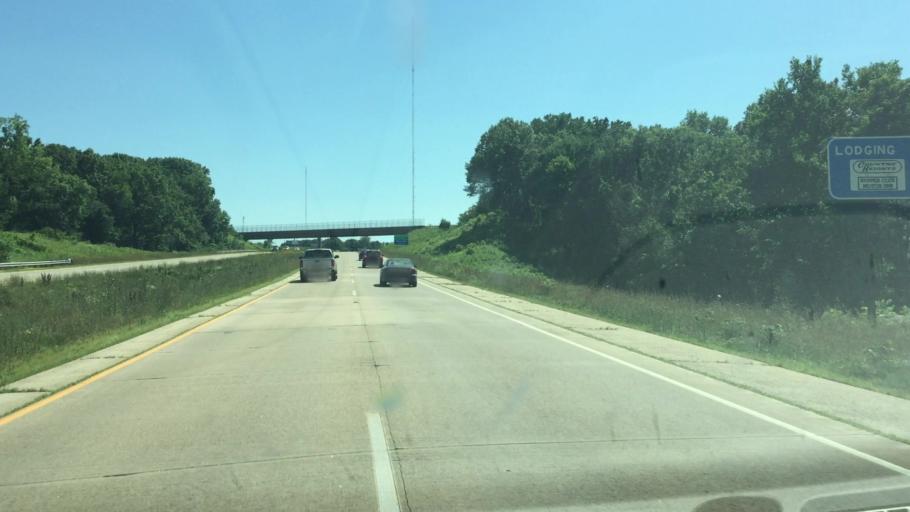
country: US
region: Illinois
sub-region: Jo Daviess County
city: East Dubuque
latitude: 42.5382
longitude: -90.6097
